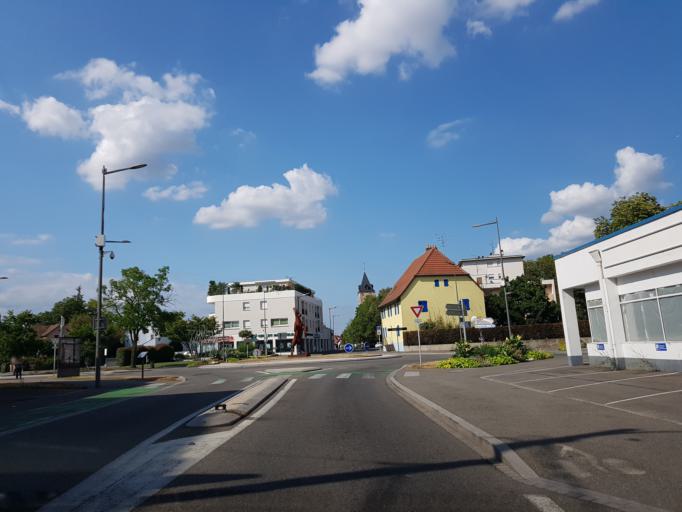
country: FR
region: Alsace
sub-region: Departement du Haut-Rhin
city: Illzach
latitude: 47.7788
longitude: 7.3474
